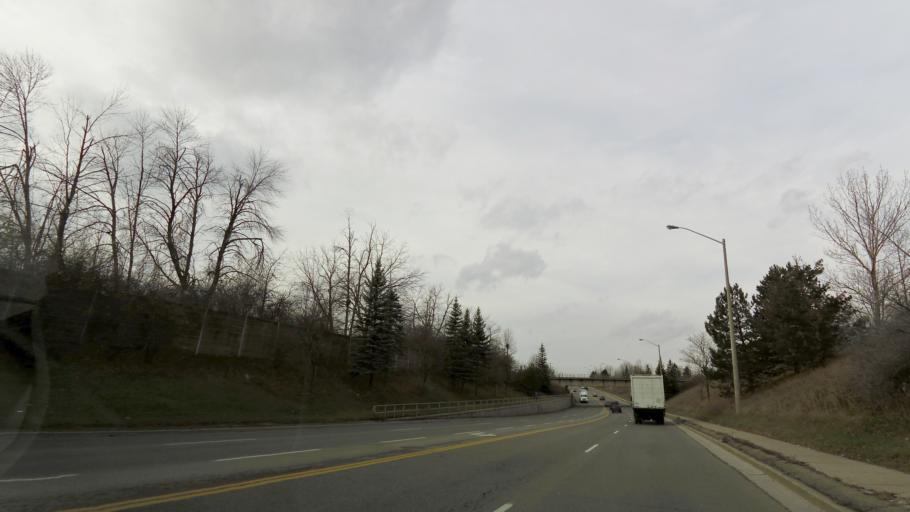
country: CA
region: Ontario
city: Etobicoke
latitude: 43.7364
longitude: -79.6380
